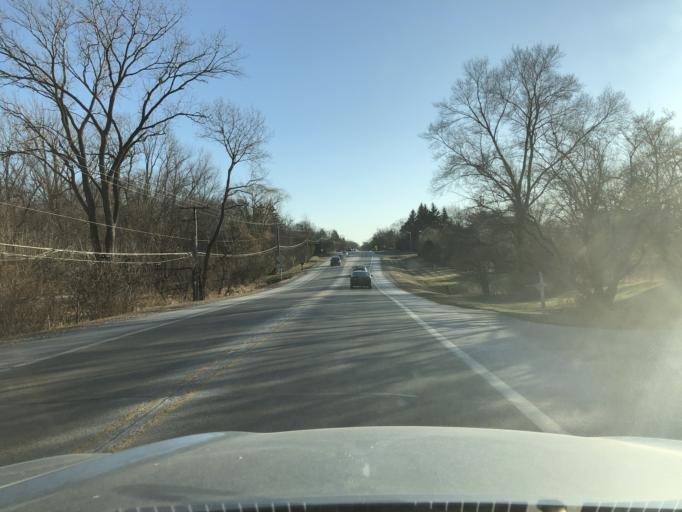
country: US
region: Illinois
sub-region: Lake County
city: Deer Park
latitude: 42.1601
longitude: -88.1018
